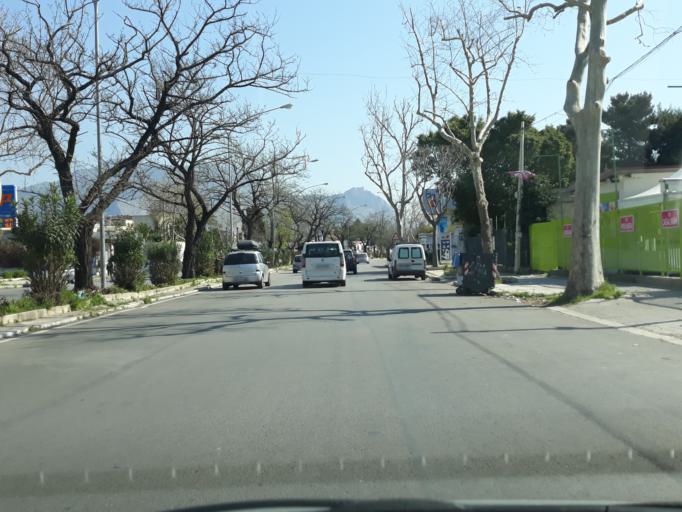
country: IT
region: Sicily
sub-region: Palermo
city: Palermo
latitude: 38.1361
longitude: 13.3165
